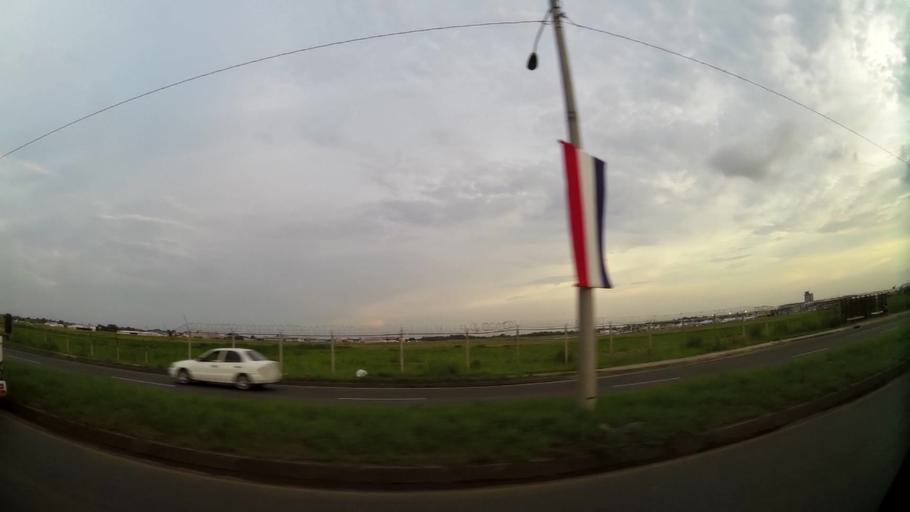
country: PA
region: Panama
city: Tocumen
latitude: 9.0759
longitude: -79.3877
